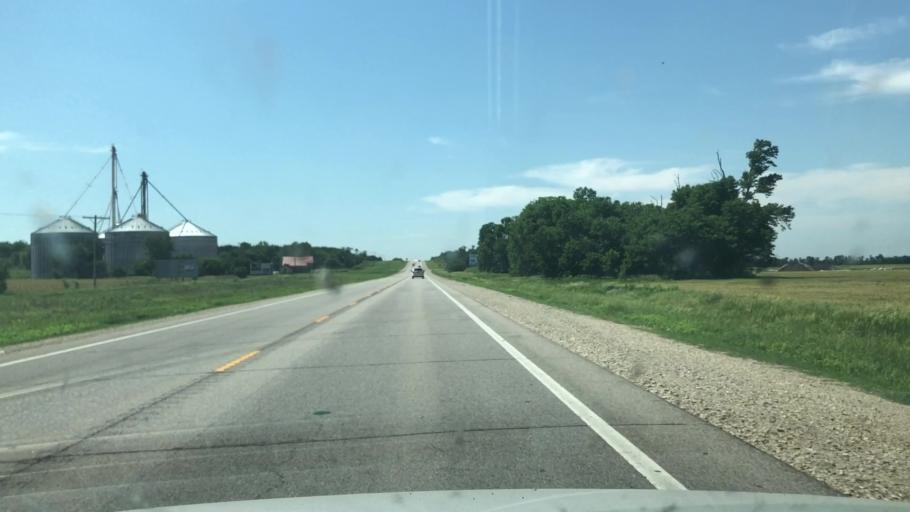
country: US
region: Kansas
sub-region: Butler County
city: Douglass
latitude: 37.3797
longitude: -97.0070
